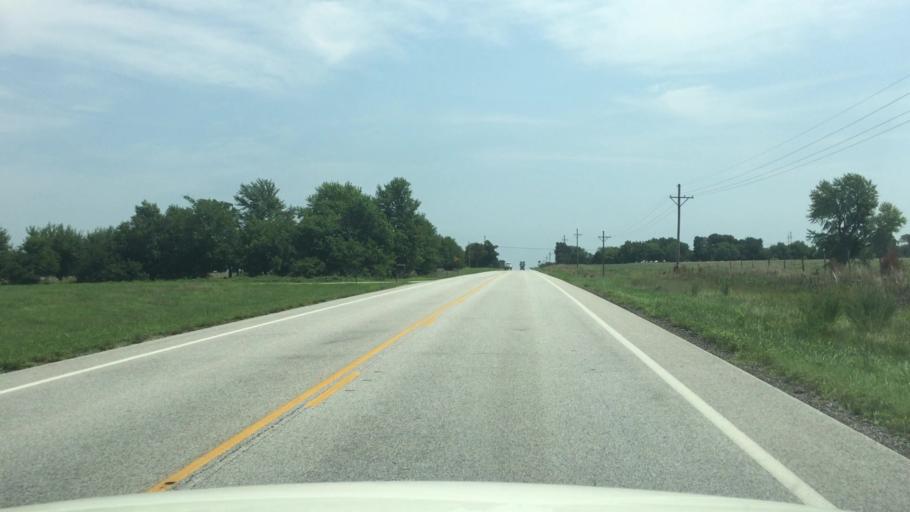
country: US
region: Kansas
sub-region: Cherokee County
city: Columbus
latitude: 37.1780
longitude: -94.7877
